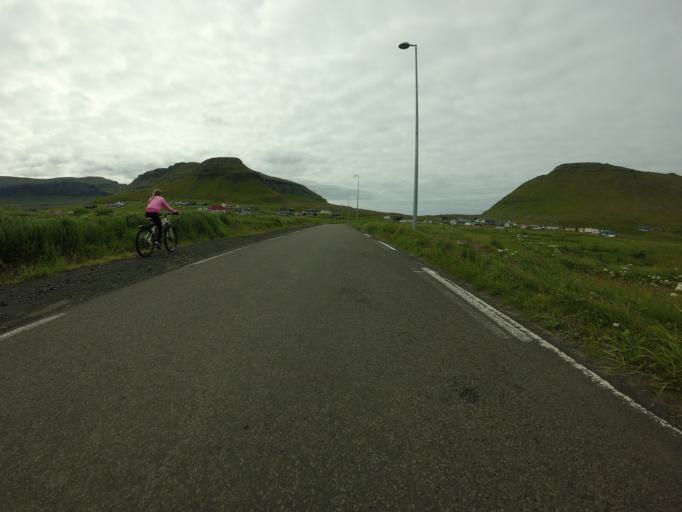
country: FO
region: Suduroy
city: Tvoroyri
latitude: 61.6014
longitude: -6.9525
